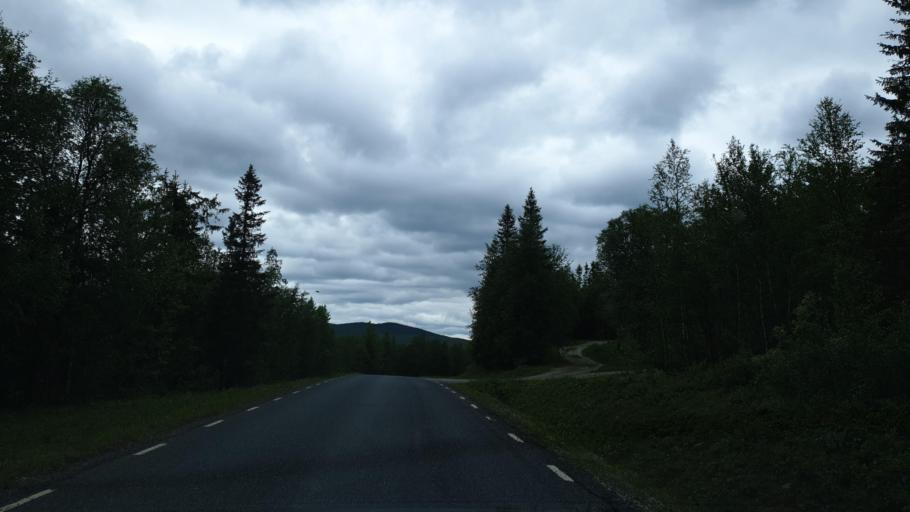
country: SE
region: Vaesterbotten
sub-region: Vilhelmina Kommun
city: Sjoberg
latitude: 65.2824
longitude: 15.2997
